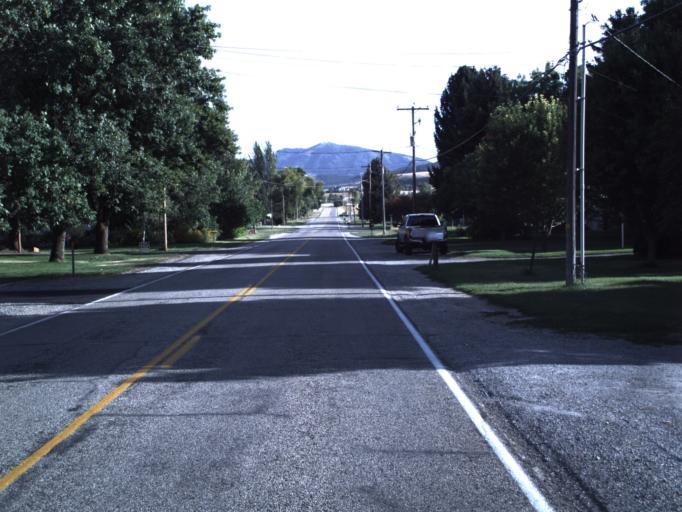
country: US
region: Utah
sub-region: Cache County
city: Wellsville
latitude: 41.6255
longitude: -111.9349
